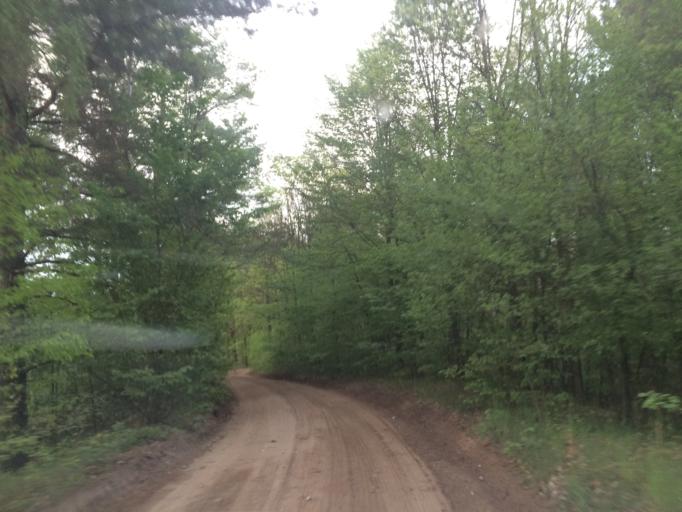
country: PL
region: Warmian-Masurian Voivodeship
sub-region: Powiat nowomiejski
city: Kurzetnik
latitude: 53.3631
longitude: 19.5184
